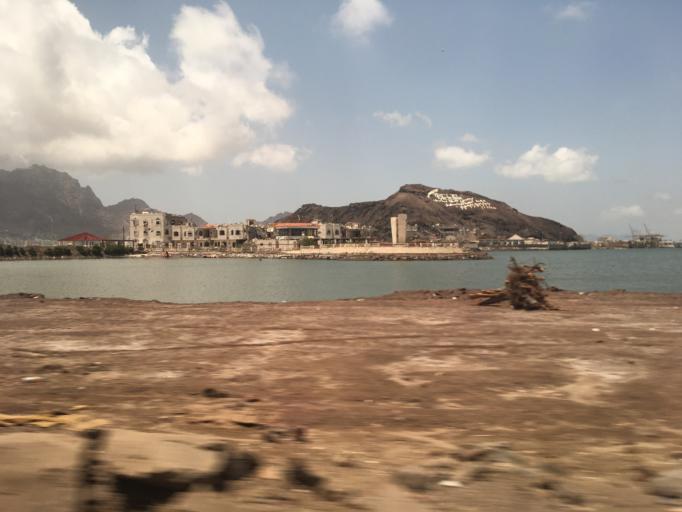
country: YE
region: Aden
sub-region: Khur Maksar
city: Khawr Maksar
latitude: 12.8119
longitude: 45.0233
